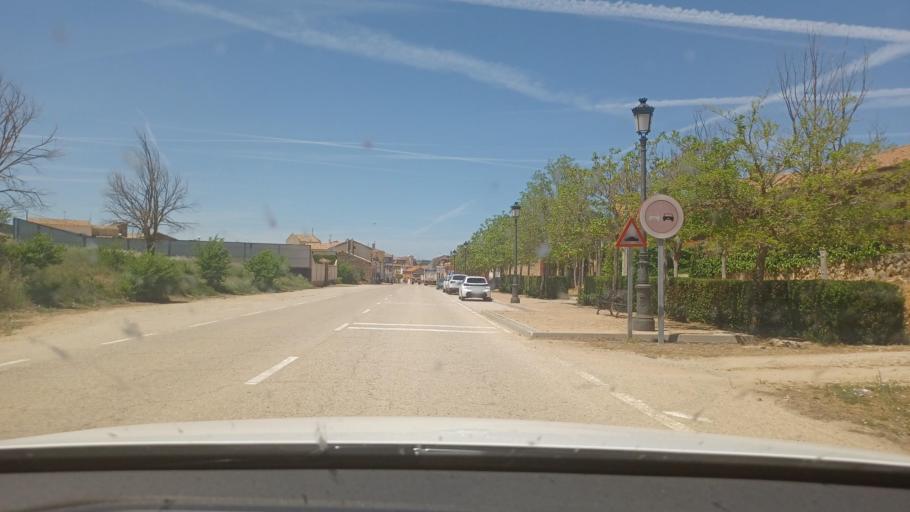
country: ES
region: Castille-La Mancha
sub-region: Provincia de Cuenca
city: Villares del Saz
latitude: 39.8379
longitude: -2.5006
